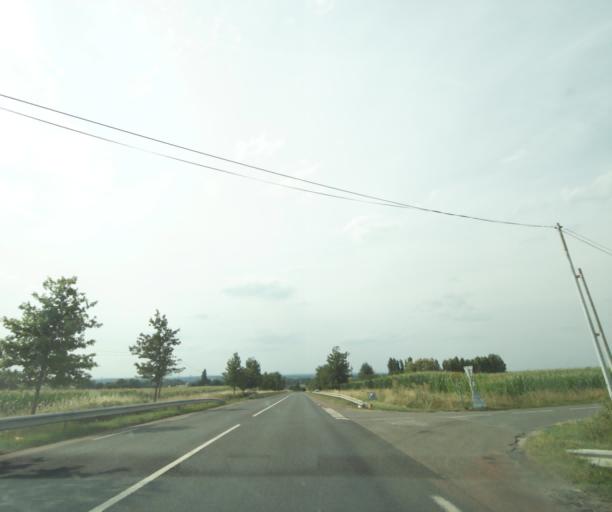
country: FR
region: Pays de la Loire
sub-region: Departement de la Sarthe
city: Ecommoy
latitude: 47.8441
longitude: 0.2594
